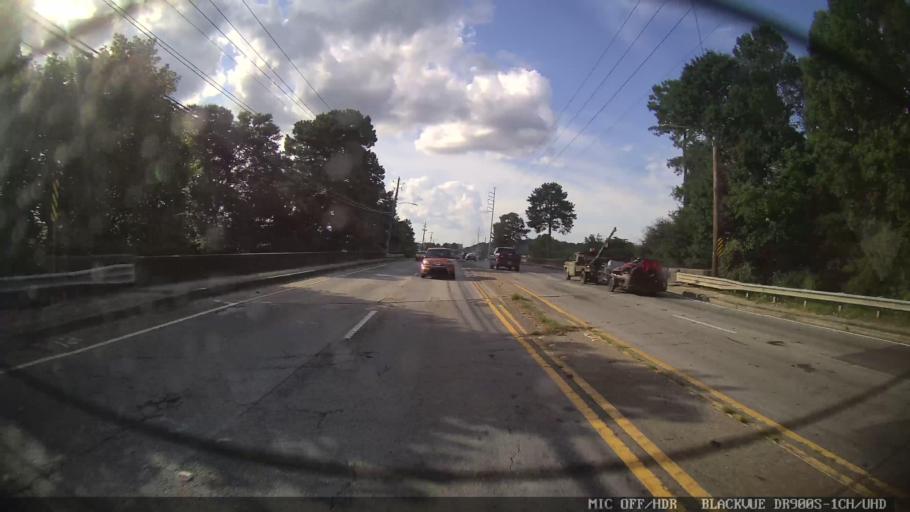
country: US
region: Georgia
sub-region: Floyd County
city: Rome
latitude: 34.2483
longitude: -85.1620
